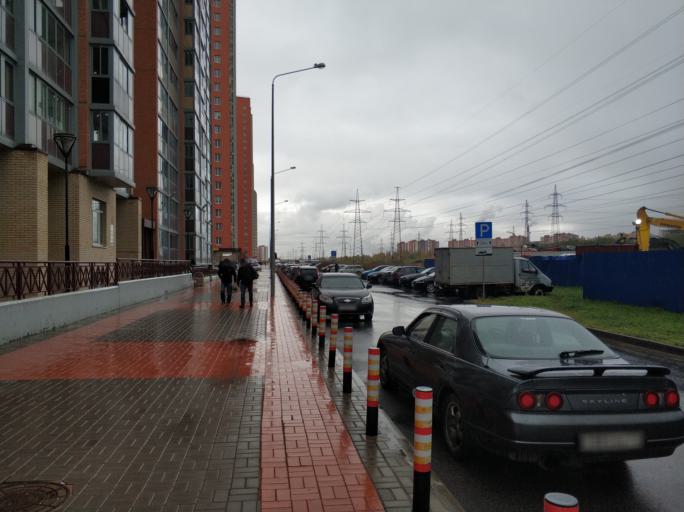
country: RU
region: Leningrad
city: Murino
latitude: 60.0562
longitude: 30.4417
